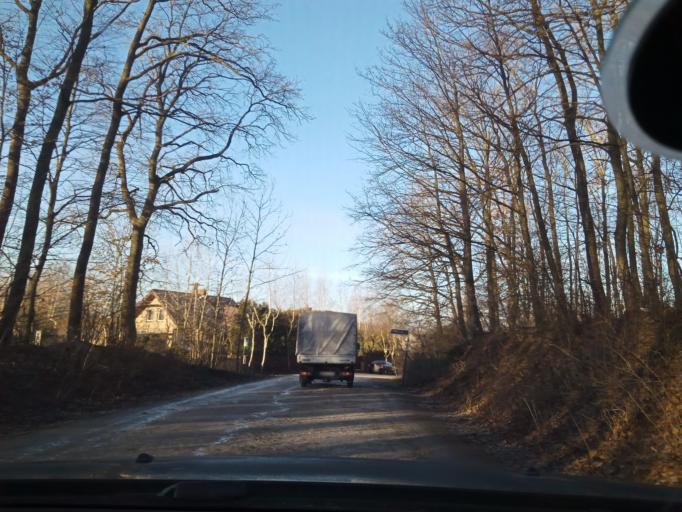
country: PL
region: Lesser Poland Voivodeship
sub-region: Powiat krakowski
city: Michalowice
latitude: 50.1896
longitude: 20.0285
